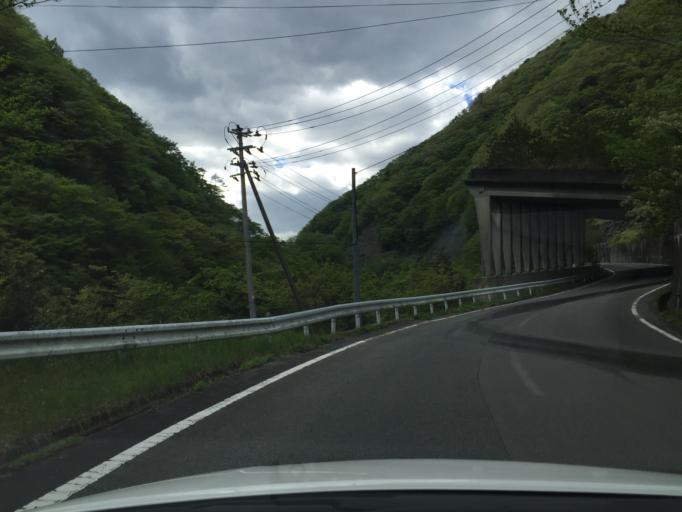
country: JP
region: Miyagi
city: Marumori
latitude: 37.7152
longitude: 140.8438
